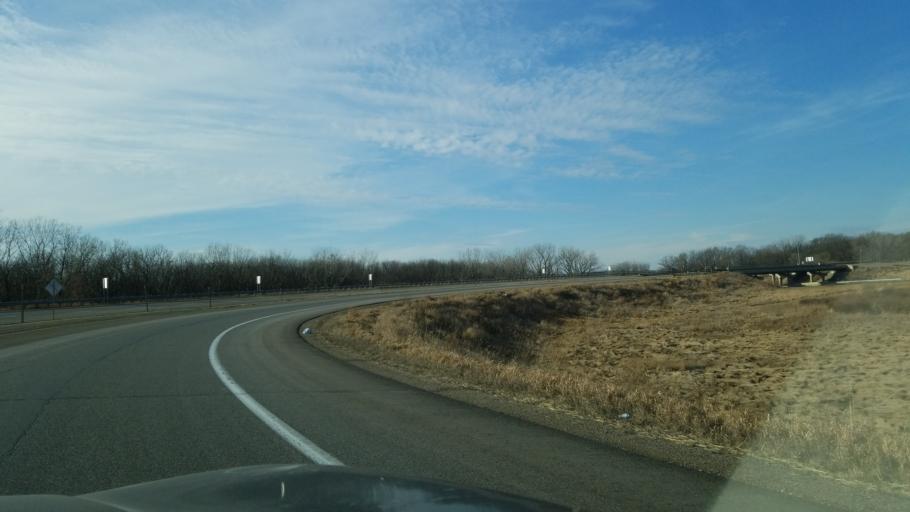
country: US
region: Iowa
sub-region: Linn County
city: Ely
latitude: 41.9248
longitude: -91.5389
